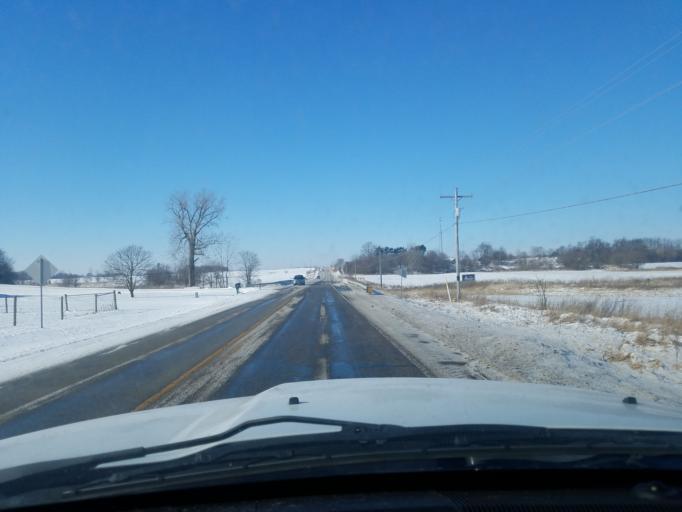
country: US
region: Indiana
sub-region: Noble County
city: Albion
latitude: 41.3958
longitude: -85.3847
